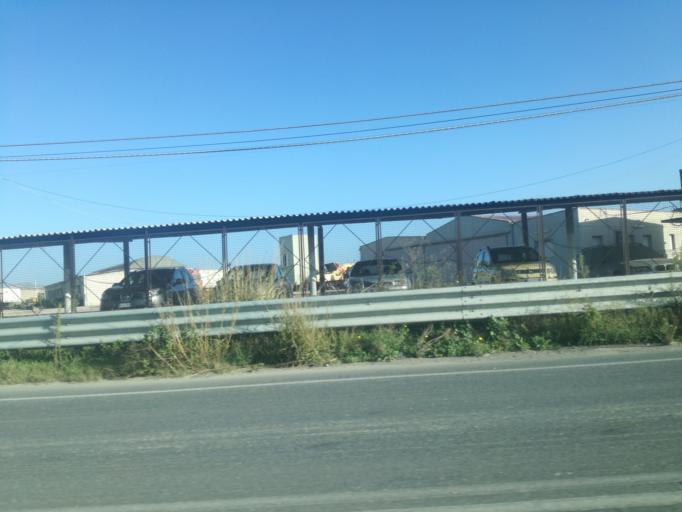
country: IT
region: Sicily
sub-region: Provincia di Caltanissetta
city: Gela
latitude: 37.0613
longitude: 14.2750
